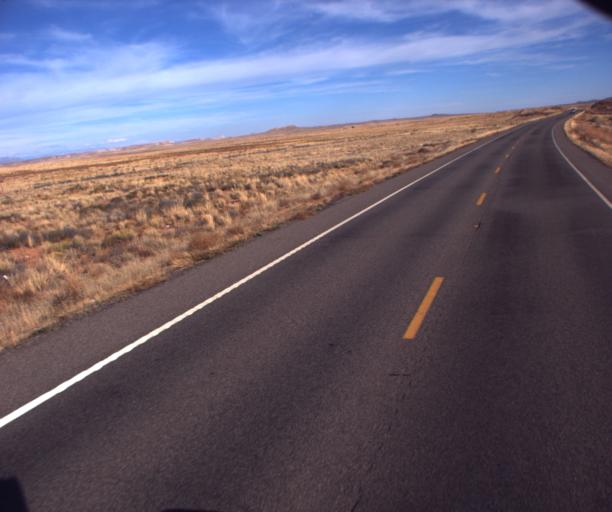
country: US
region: Arizona
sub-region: Apache County
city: Lukachukai
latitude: 36.9579
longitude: -109.3071
